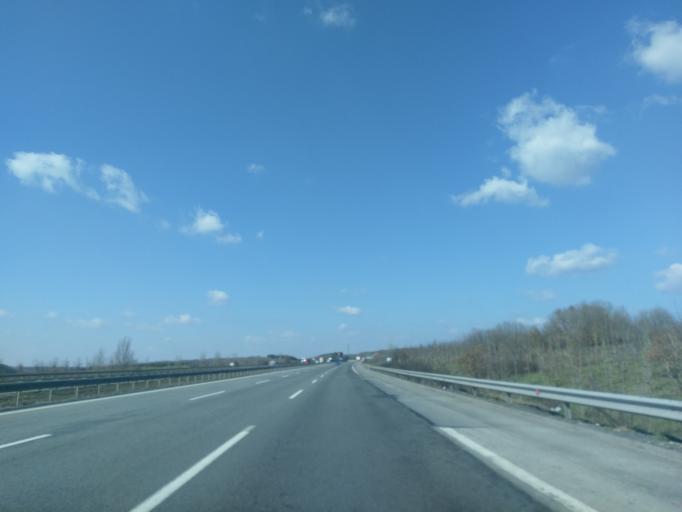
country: TR
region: Istanbul
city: Canta
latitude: 41.1759
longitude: 28.1165
